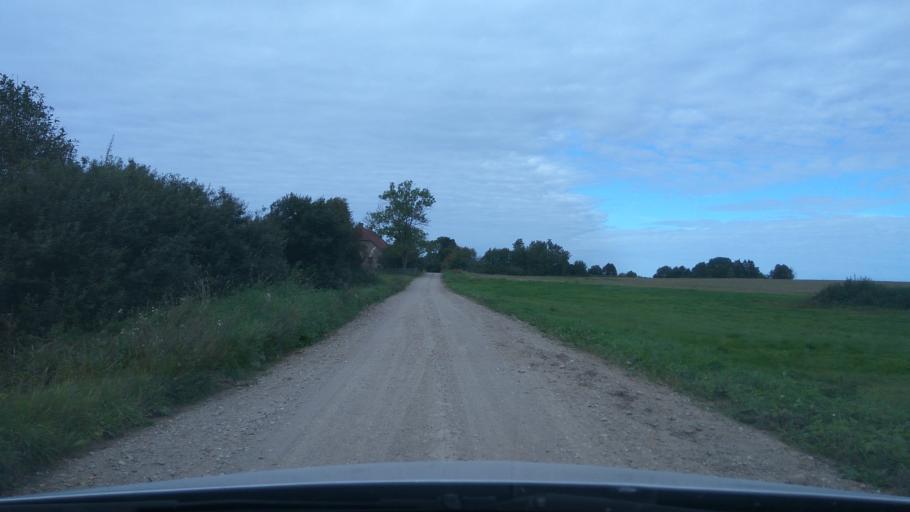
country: LV
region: Kuldigas Rajons
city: Kuldiga
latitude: 57.2422
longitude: 21.9491
